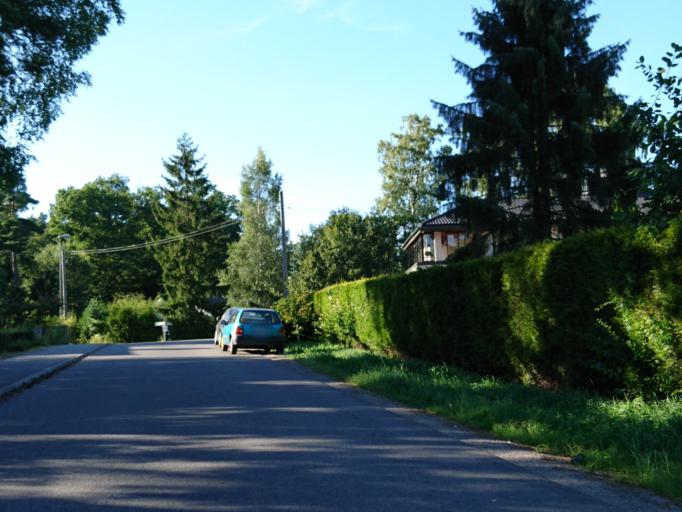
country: SE
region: Stockholm
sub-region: Huddinge Kommun
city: Segeltorp
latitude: 59.2793
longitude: 17.9333
